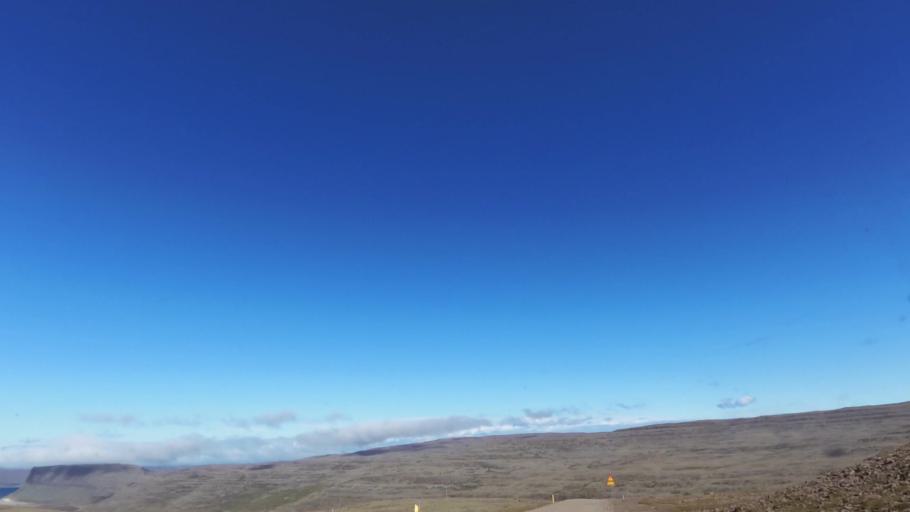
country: IS
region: West
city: Olafsvik
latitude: 65.5530
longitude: -24.2215
